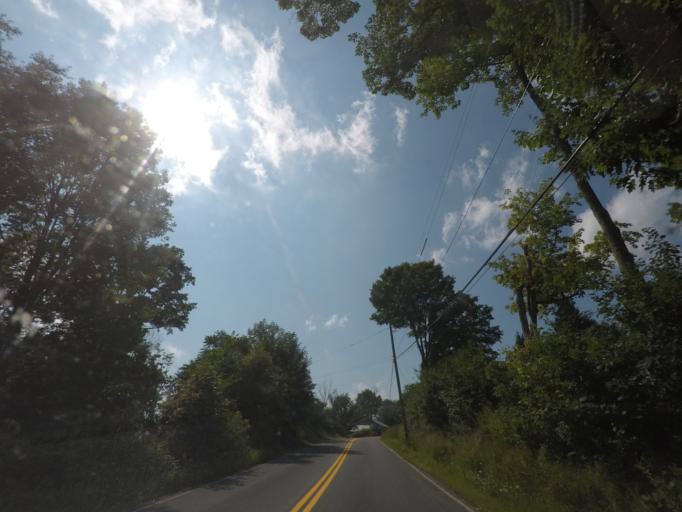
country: US
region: New York
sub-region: Rensselaer County
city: Poestenkill
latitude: 42.6882
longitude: -73.5189
